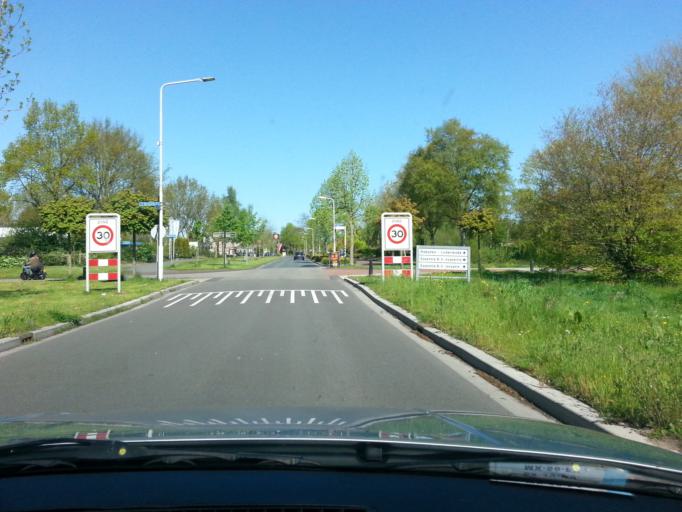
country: NL
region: Friesland
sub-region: Gemeente Achtkarspelen
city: Buitenpost
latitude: 53.2485
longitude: 6.1502
